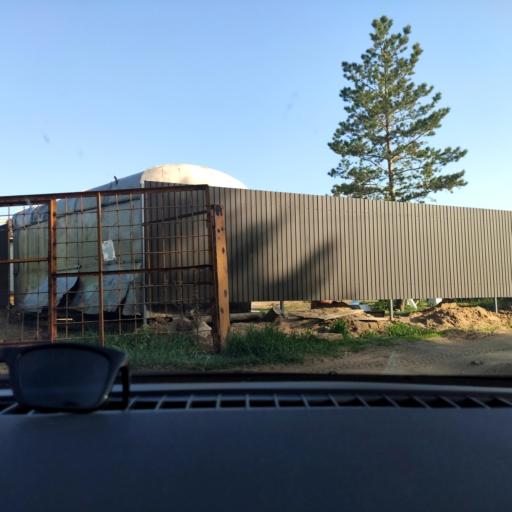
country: RU
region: Samara
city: Volzhskiy
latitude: 53.4346
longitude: 50.1603
